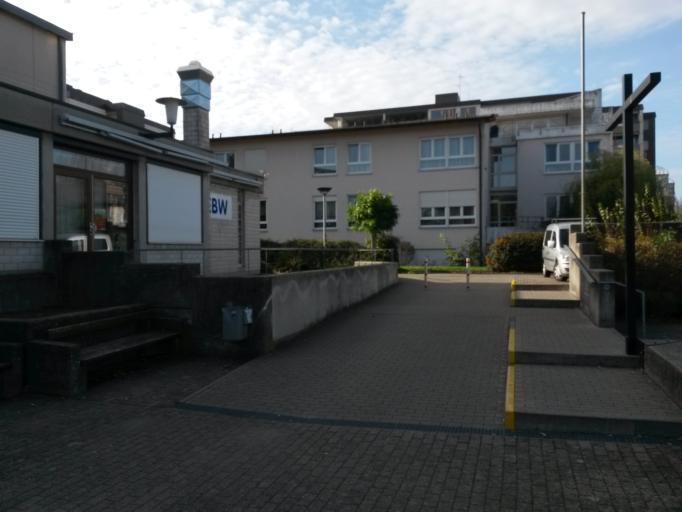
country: DE
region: Baden-Wuerttemberg
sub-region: Freiburg Region
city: Merzhausen
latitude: 47.9952
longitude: 7.8099
